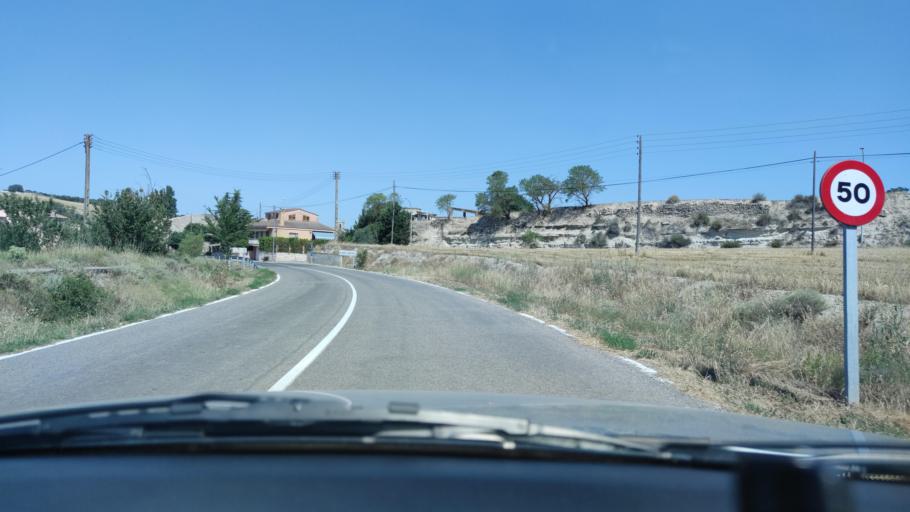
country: ES
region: Catalonia
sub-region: Provincia de Lleida
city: Sant Guim de Freixenet
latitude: 41.6269
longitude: 1.3452
